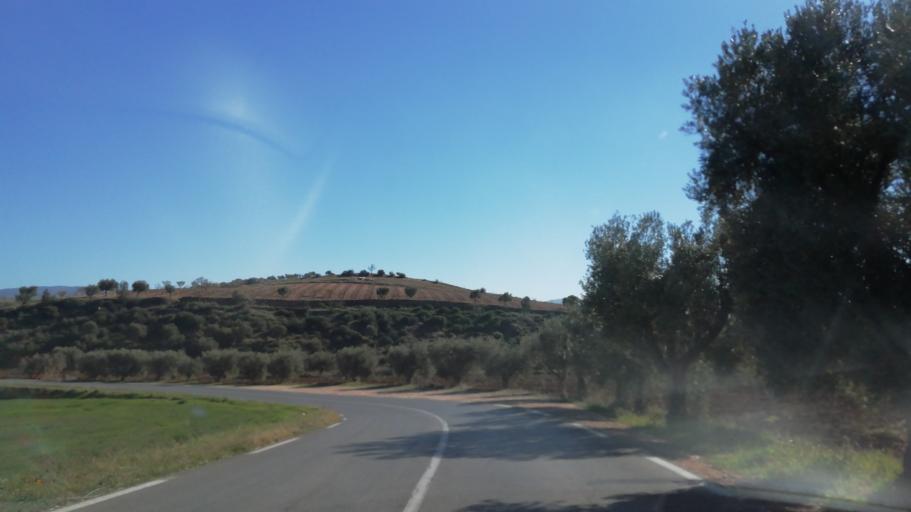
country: DZ
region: Tlemcen
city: Beni Mester
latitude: 34.8264
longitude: -1.5773
